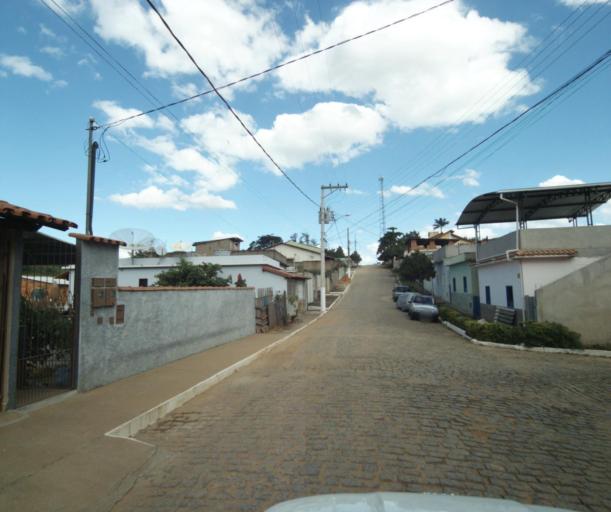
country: BR
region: Espirito Santo
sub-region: Sao Jose Do Calcado
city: Sao Jose do Calcado
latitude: -21.0310
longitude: -41.6555
